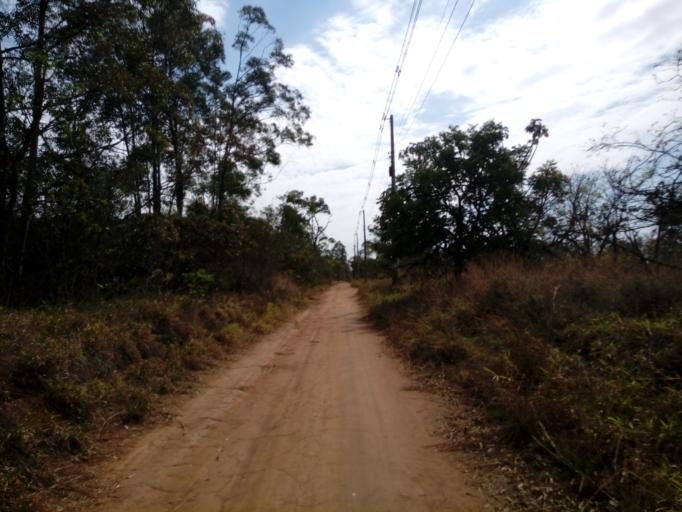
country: BR
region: Sao Paulo
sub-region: Sao Carlos
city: Sao Carlos
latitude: -21.9758
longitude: -47.8751
